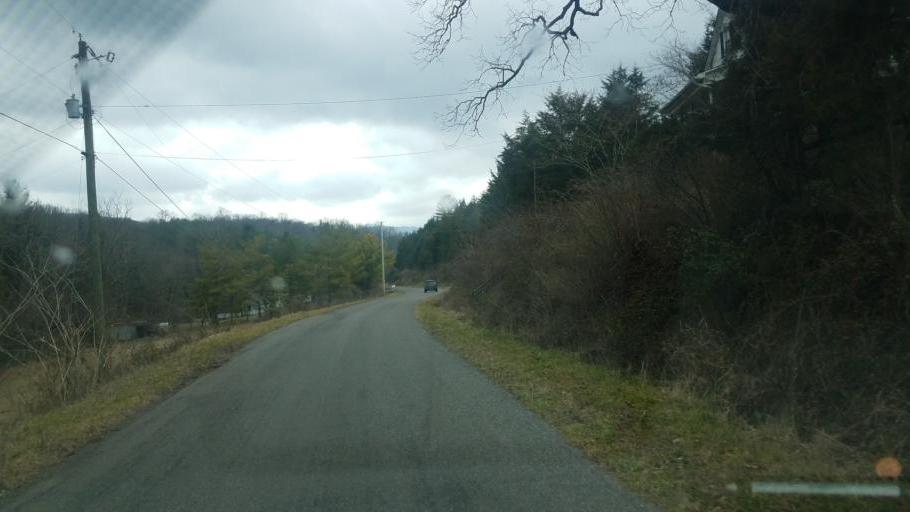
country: US
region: Virginia
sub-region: Giles County
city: Pembroke
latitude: 37.2347
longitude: -80.6931
